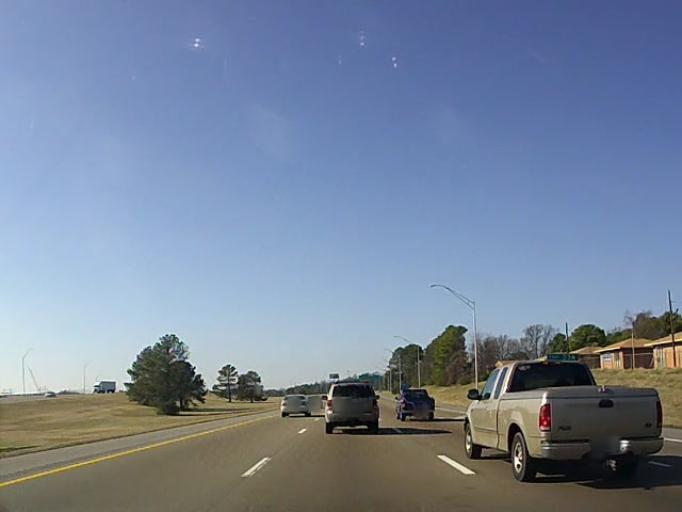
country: US
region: Tennessee
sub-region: Shelby County
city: New South Memphis
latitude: 35.0767
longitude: -89.9810
